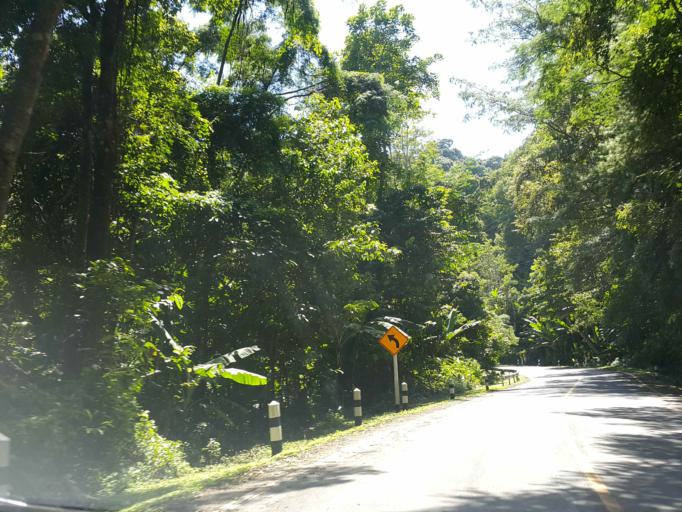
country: TH
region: Chiang Mai
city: Mae Chaem
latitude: 18.5443
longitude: 98.5326
